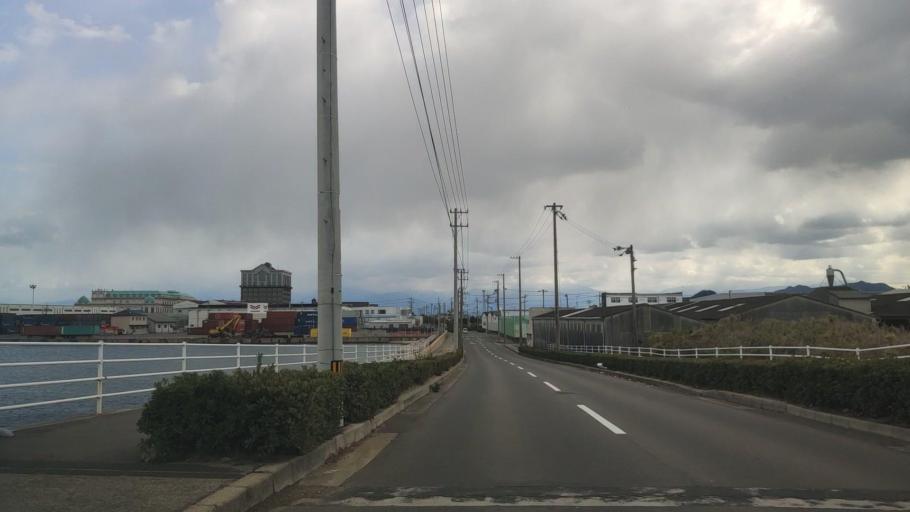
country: JP
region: Ehime
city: Saijo
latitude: 34.0515
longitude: 133.0237
